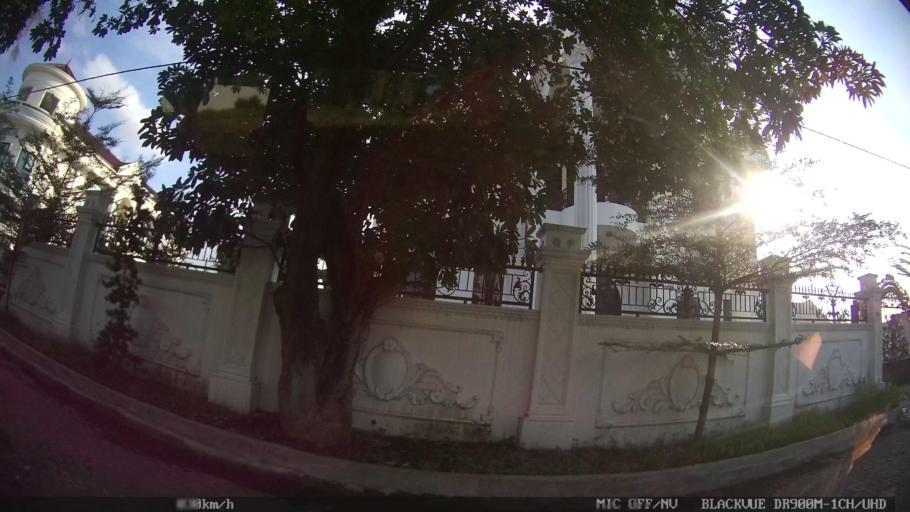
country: ID
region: North Sumatra
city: Medan
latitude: 3.6213
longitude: 98.6499
